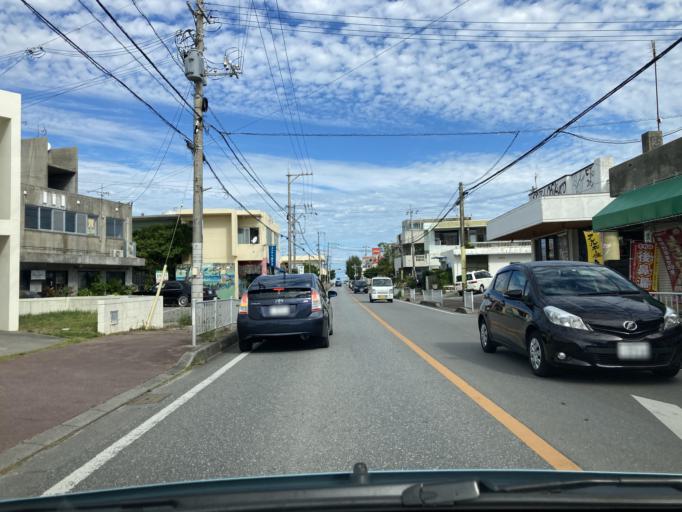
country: JP
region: Okinawa
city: Ishikawa
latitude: 26.4127
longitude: 127.7323
